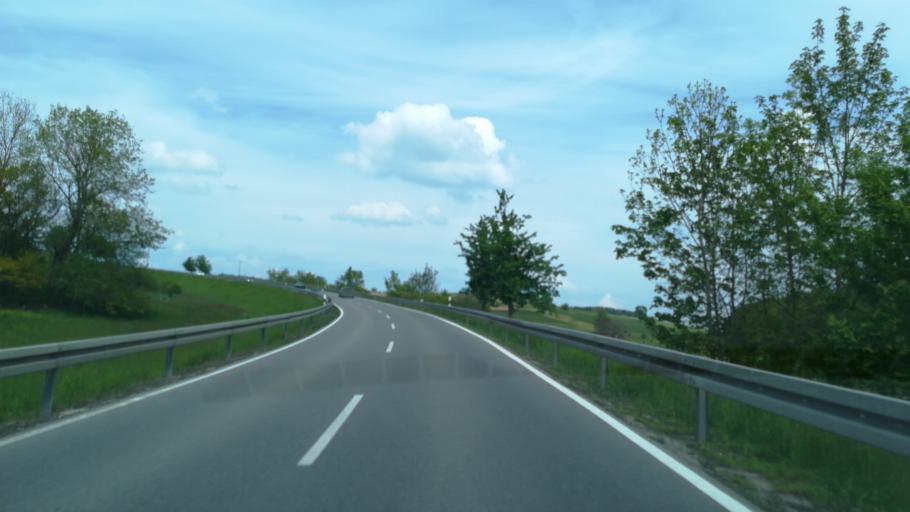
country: DE
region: Baden-Wuerttemberg
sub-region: Freiburg Region
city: Stockach
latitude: 47.8730
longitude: 9.0340
